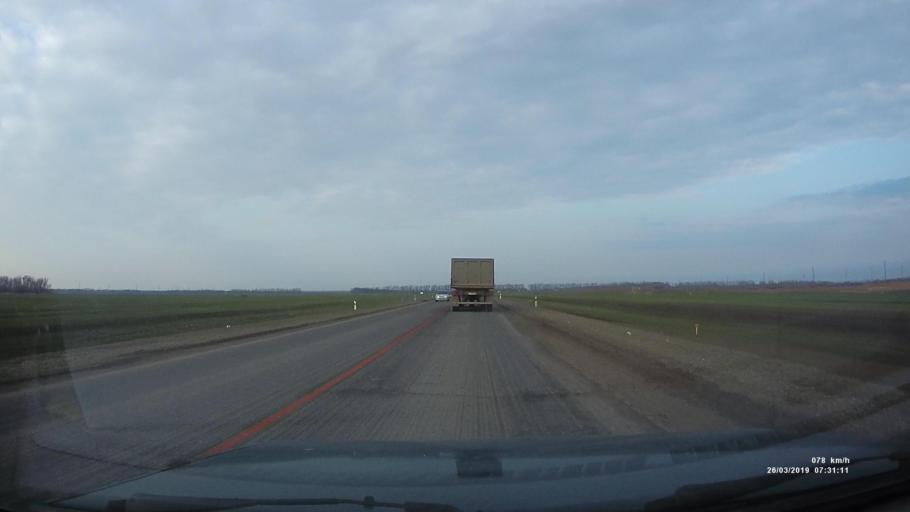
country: RU
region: Rostov
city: Novobessergenovka
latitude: 47.2338
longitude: 38.7952
